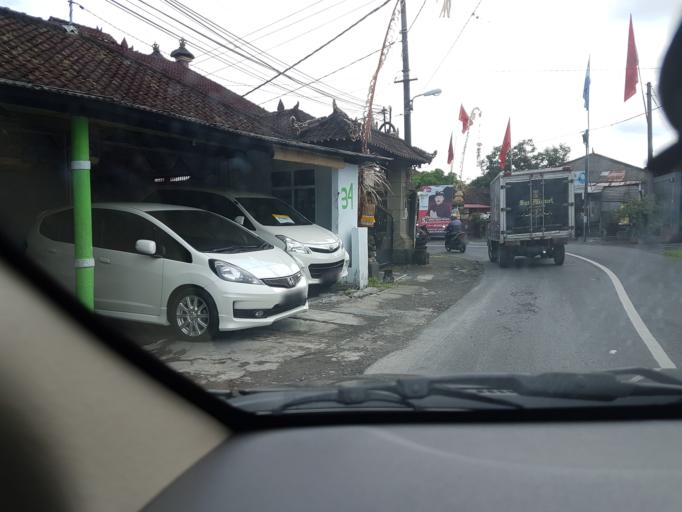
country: ID
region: Bali
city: Denpasar
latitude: -8.6666
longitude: 115.1918
